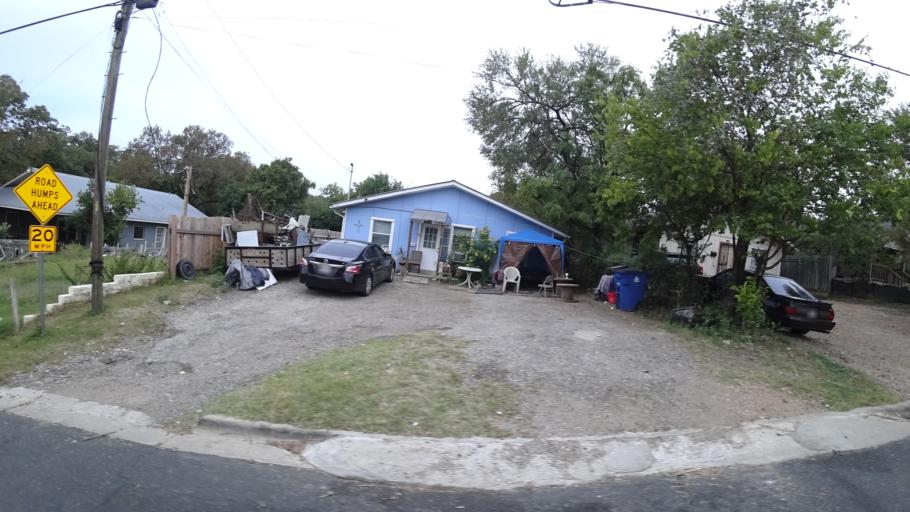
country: US
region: Texas
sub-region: Travis County
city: Austin
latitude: 30.2695
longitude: -97.7164
